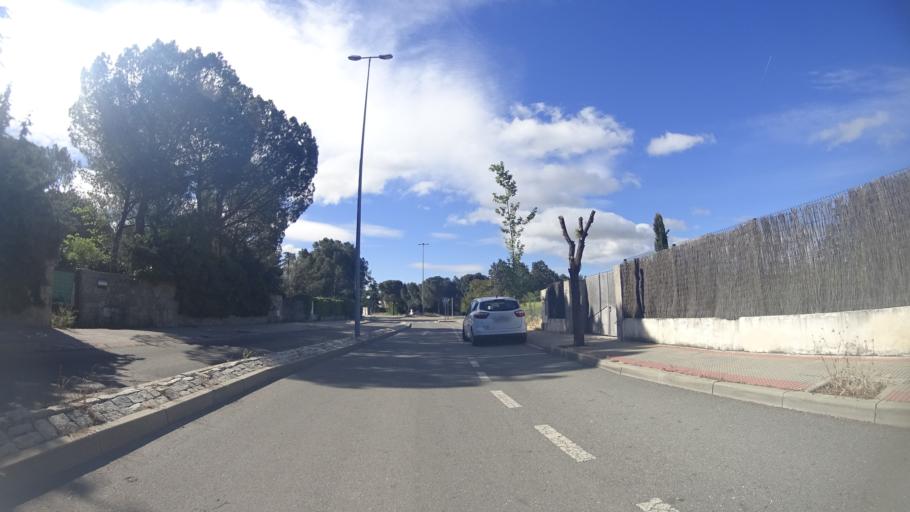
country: ES
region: Madrid
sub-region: Provincia de Madrid
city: Villanueva del Pardillo
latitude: 40.4898
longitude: -3.9402
